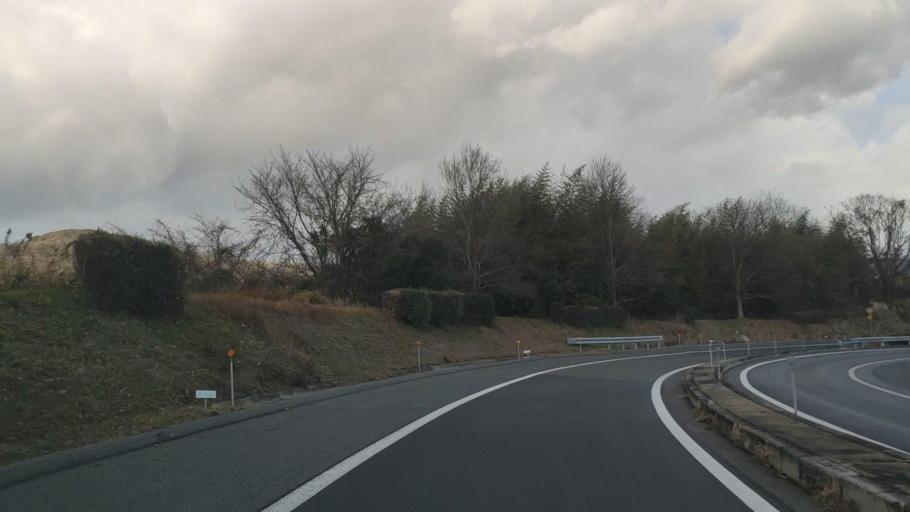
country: JP
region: Hiroshima
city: Onomichi
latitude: 34.4625
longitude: 133.2379
